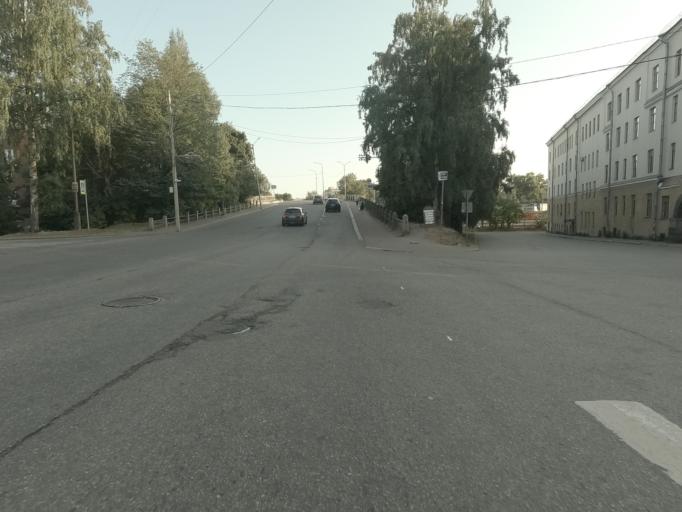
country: RU
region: Leningrad
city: Vyborg
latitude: 60.7164
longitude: 28.7585
